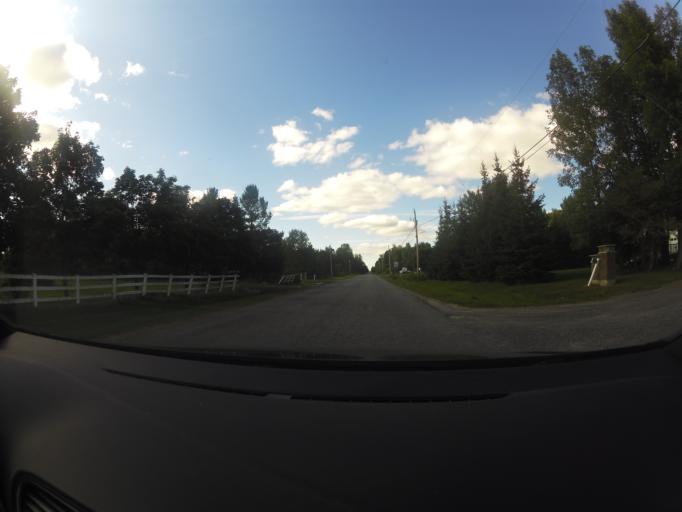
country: CA
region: Ontario
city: Carleton Place
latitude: 45.1327
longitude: -76.0749
